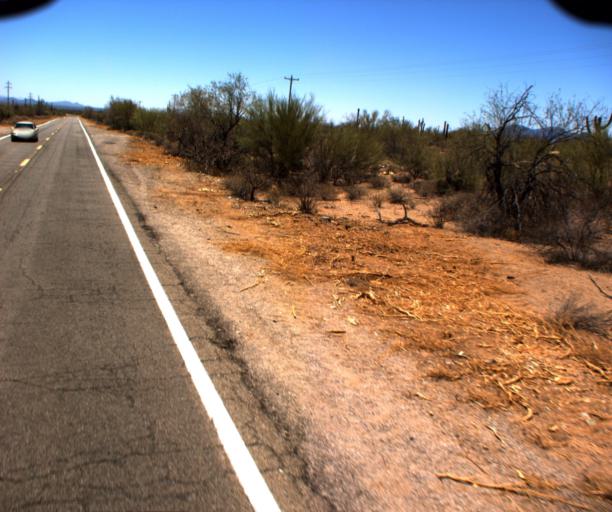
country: US
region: Arizona
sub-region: Pima County
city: Sells
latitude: 32.1491
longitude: -112.1039
